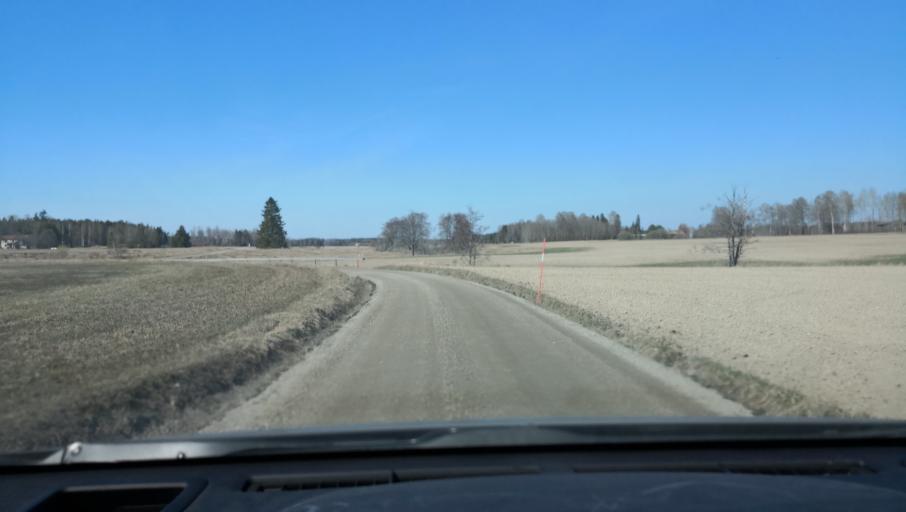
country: SE
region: Vaestmanland
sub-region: Sala Kommun
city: Sala
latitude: 59.8803
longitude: 16.5322
